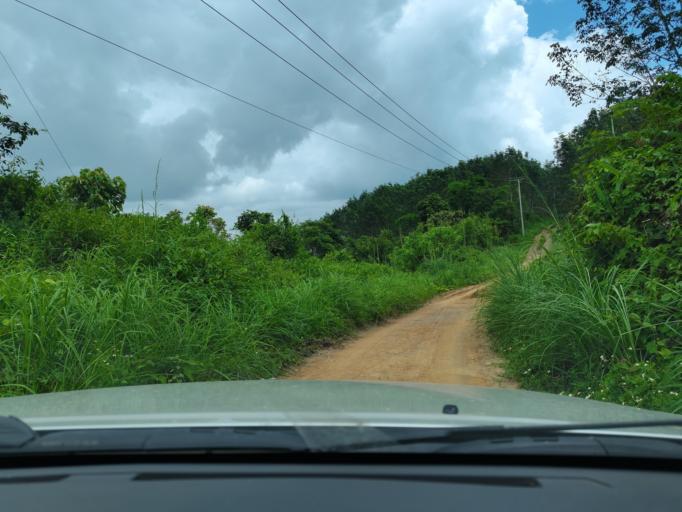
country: LA
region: Loungnamtha
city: Muang Long
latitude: 20.6971
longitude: 101.0388
